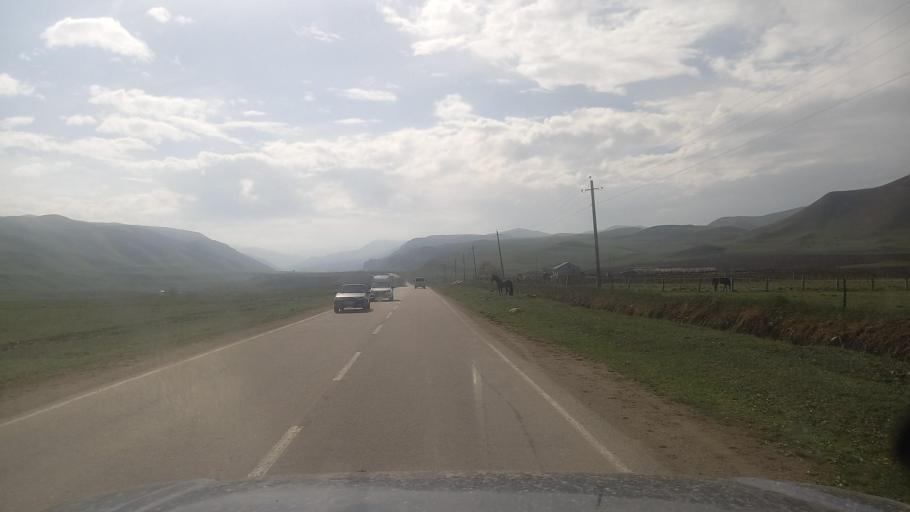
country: RU
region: Kabardino-Balkariya
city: Kamennomostskoye
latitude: 43.7360
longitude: 43.0064
